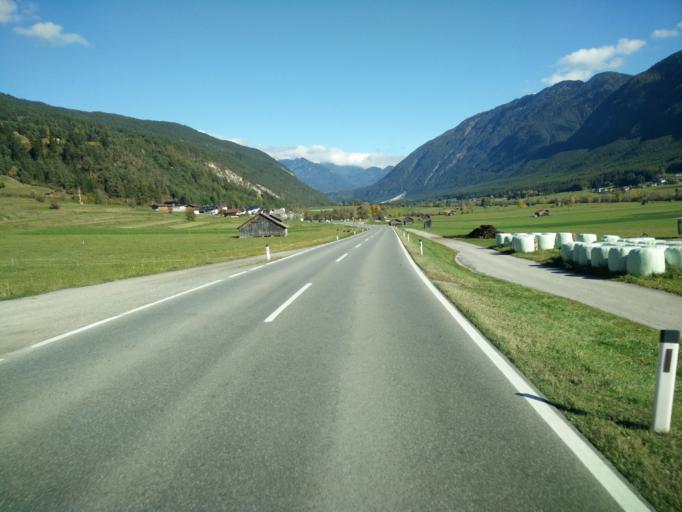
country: AT
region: Tyrol
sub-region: Politischer Bezirk Imst
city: Tarrenz
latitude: 47.2674
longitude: 10.7714
